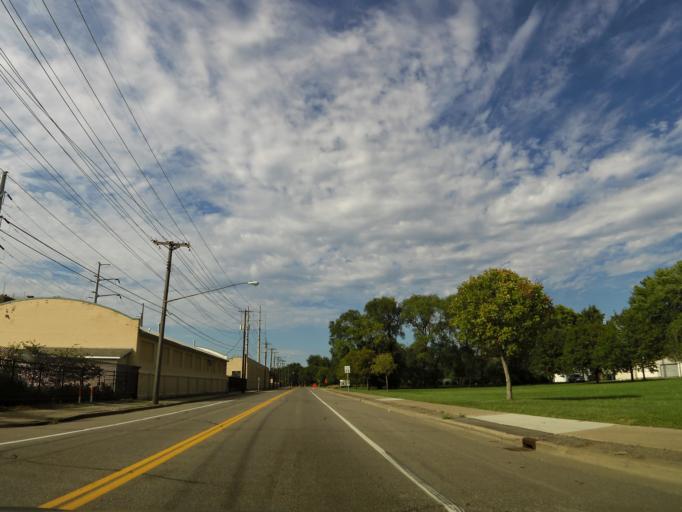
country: US
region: Minnesota
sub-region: Anoka County
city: Columbia Heights
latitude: 45.0189
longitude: -93.2725
